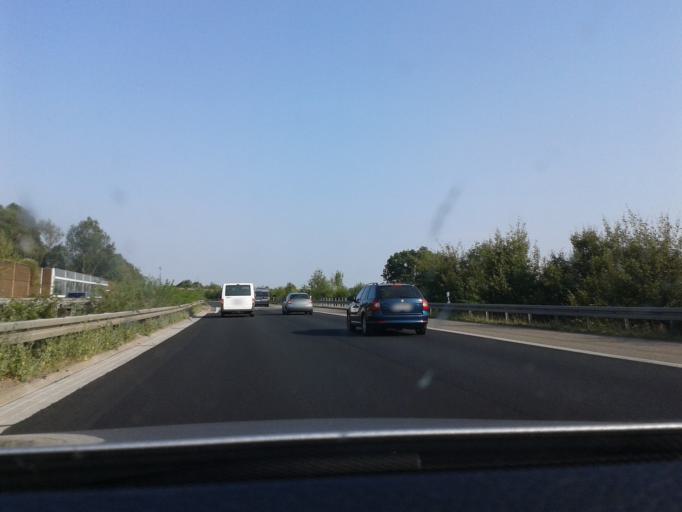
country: DE
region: Saxony-Anhalt
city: Wallhausen
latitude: 51.4566
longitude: 11.1954
